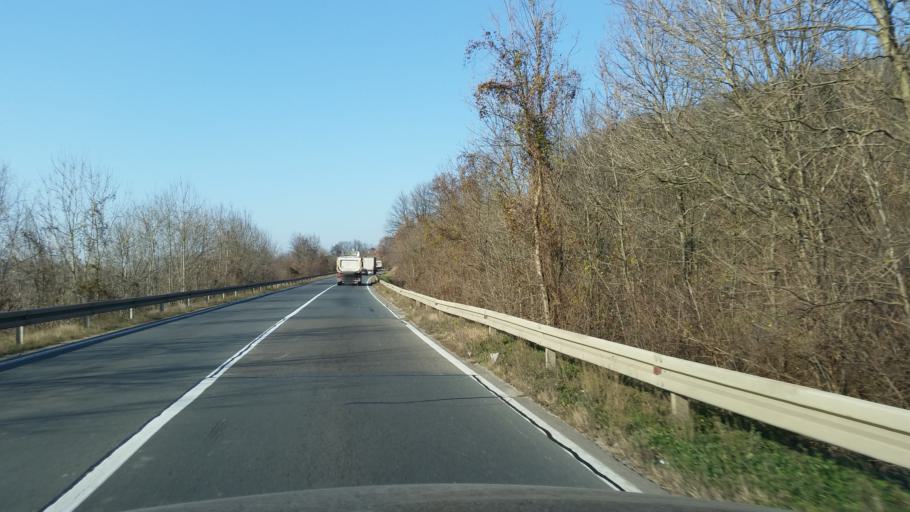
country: RS
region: Central Serbia
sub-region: Kolubarski Okrug
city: Lajkovac
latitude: 44.3453
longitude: 20.1987
